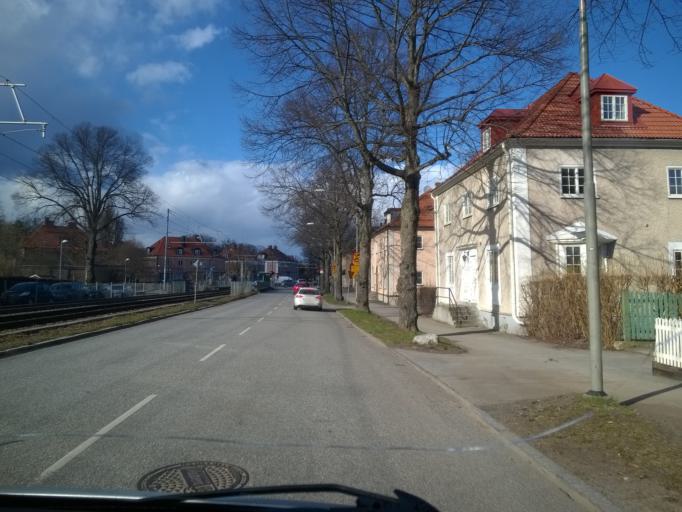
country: SE
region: Stockholm
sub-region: Sundbybergs Kommun
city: Sundbyberg
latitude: 59.3281
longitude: 17.9740
